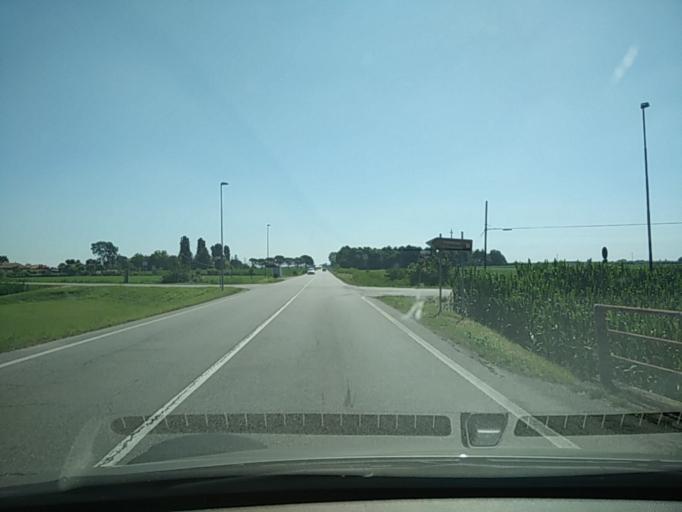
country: IT
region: Veneto
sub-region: Provincia di Venezia
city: Ceggia
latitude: 45.6361
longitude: 12.6564
